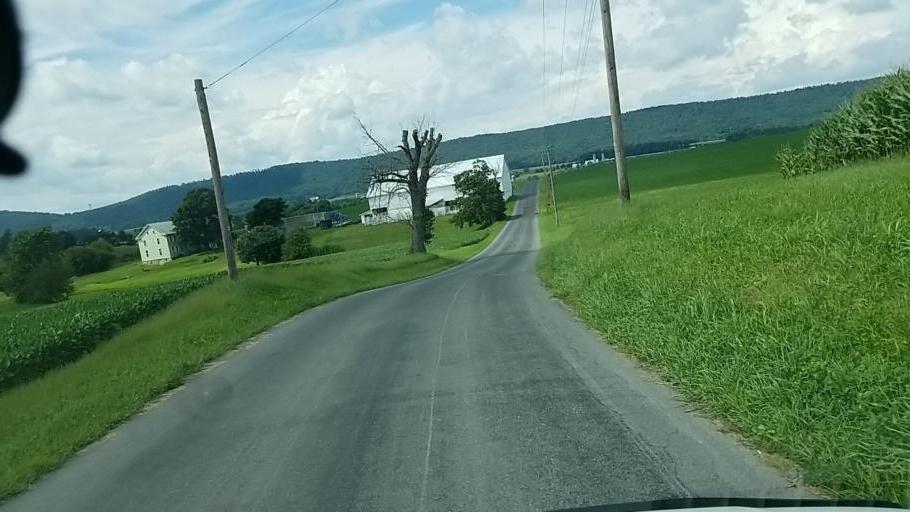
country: US
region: Pennsylvania
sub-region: Dauphin County
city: Elizabethville
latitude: 40.5884
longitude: -76.8452
